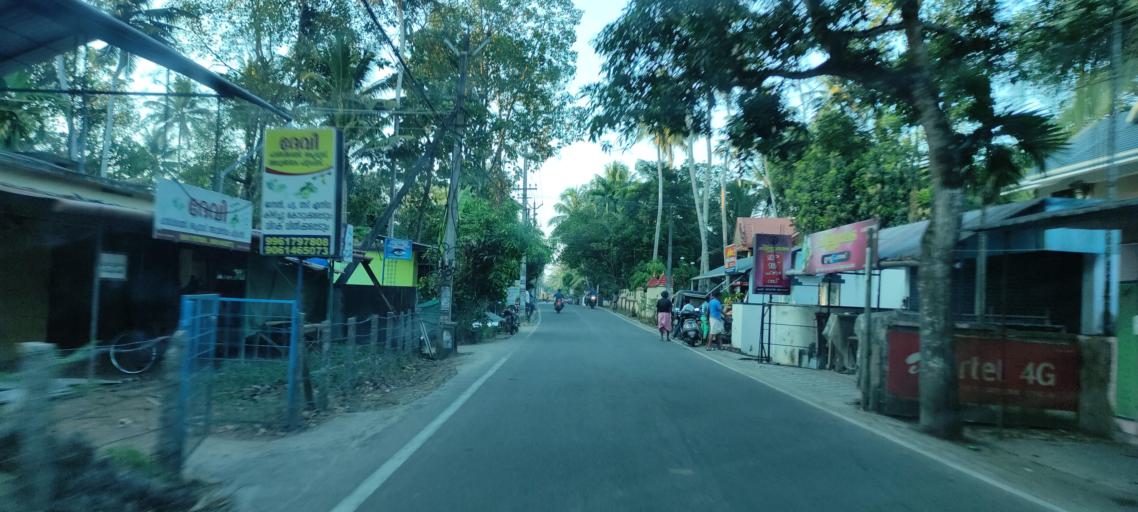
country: IN
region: Kerala
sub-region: Alappuzha
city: Kayankulam
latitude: 9.2225
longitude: 76.4601
